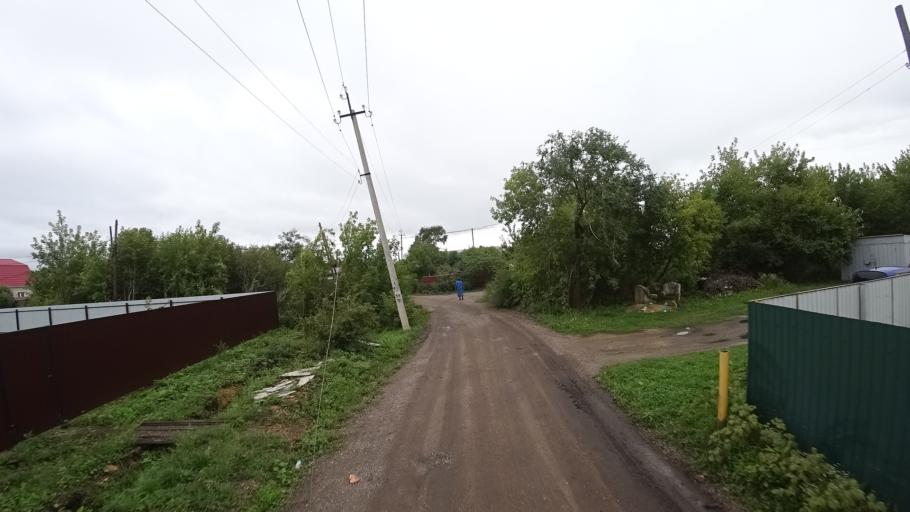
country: RU
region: Primorskiy
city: Chernigovka
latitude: 44.3371
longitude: 132.5358
